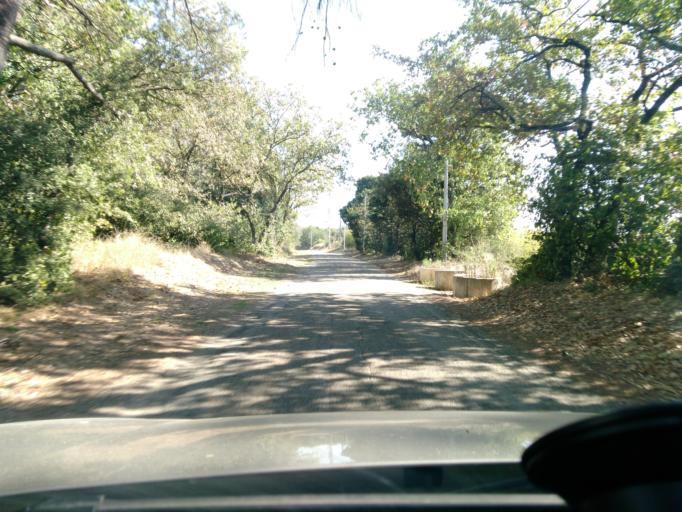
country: FR
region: Rhone-Alpes
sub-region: Departement de la Drome
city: Montboucher-sur-Jabron
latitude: 44.5560
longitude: 4.7976
